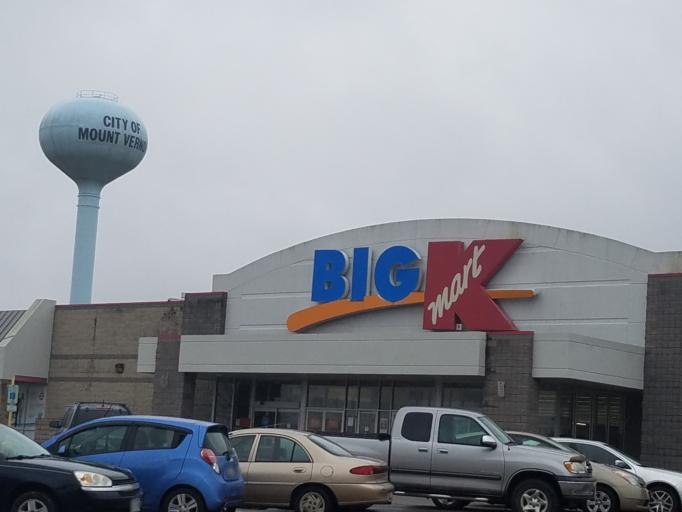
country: US
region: Ohio
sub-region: Knox County
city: Mount Vernon
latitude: 40.4009
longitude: -82.4457
